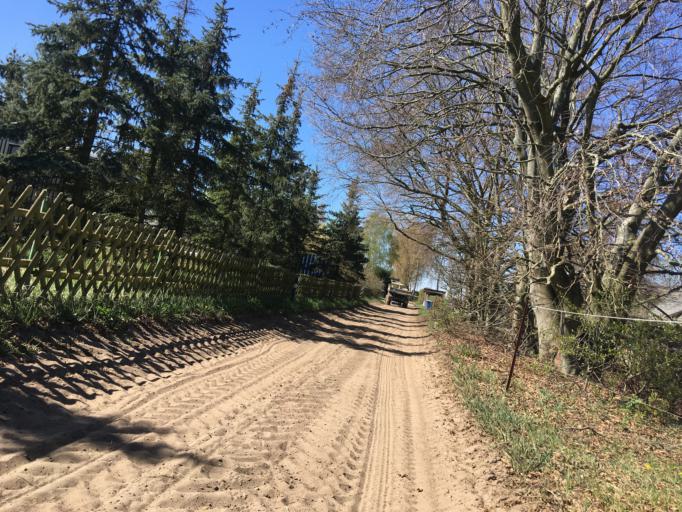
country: DE
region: Berlin
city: Buch
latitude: 52.6784
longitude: 13.4794
